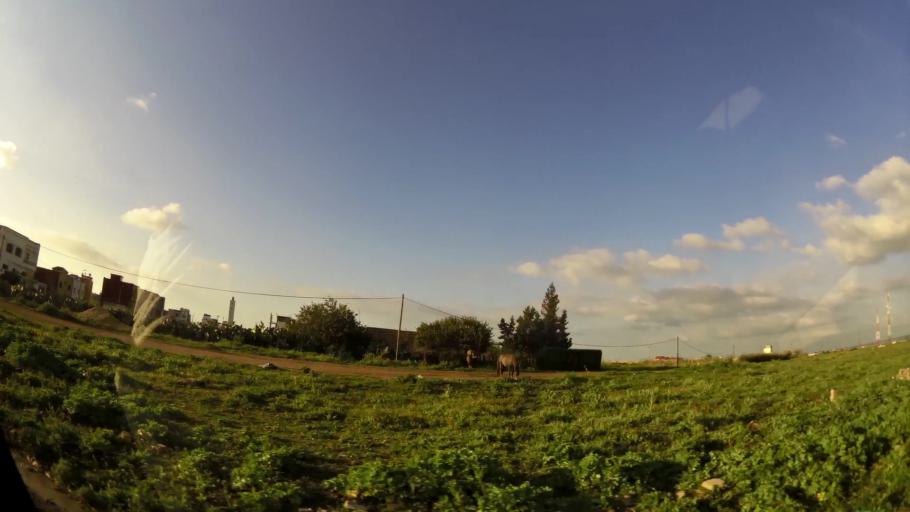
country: MA
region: Chaouia-Ouardigha
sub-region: Settat Province
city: Settat
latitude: 33.0078
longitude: -7.5948
